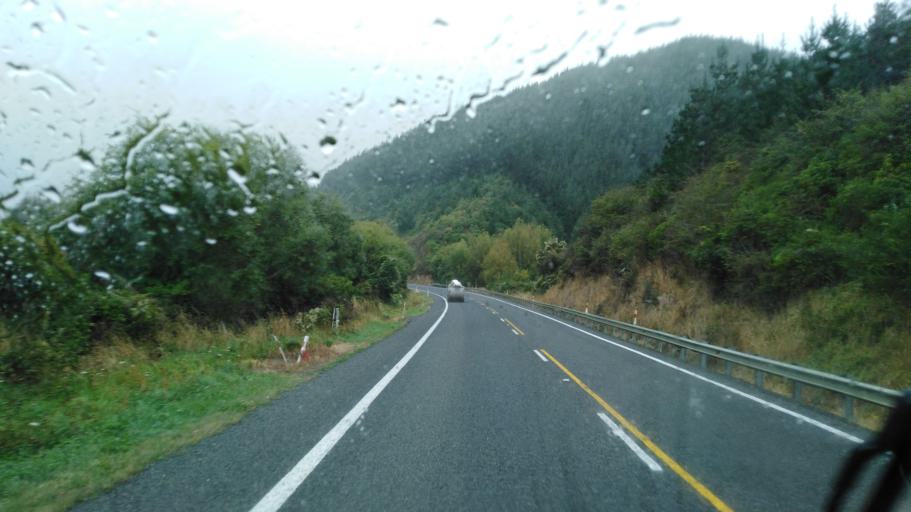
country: NZ
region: Marlborough
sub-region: Marlborough District
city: Picton
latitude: -41.3874
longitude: 173.9520
